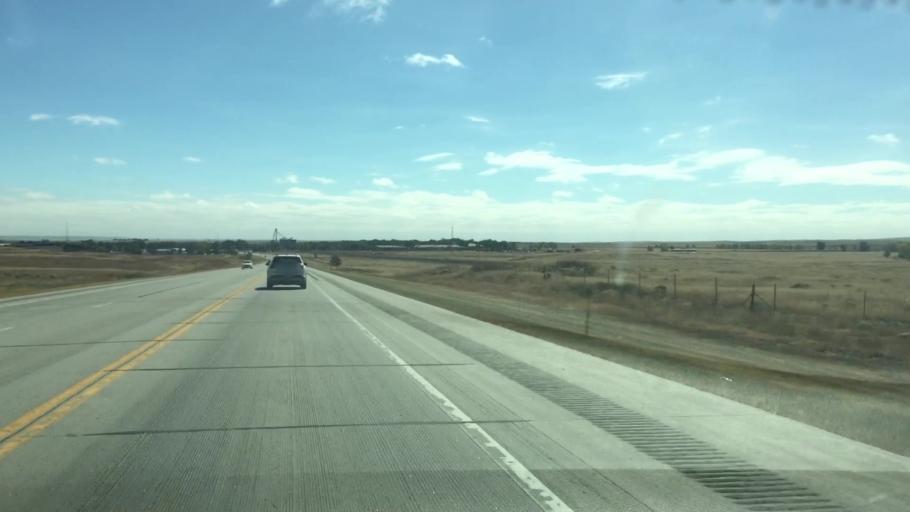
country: US
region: Colorado
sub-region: Lincoln County
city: Hugo
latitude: 39.1409
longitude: -103.4868
